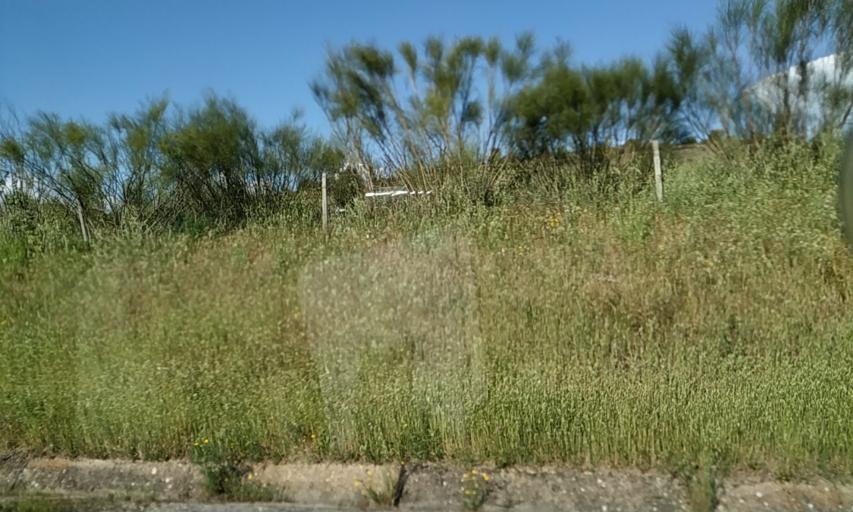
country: PT
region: Portalegre
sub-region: Portalegre
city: Urra
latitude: 39.0807
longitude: -7.4369
